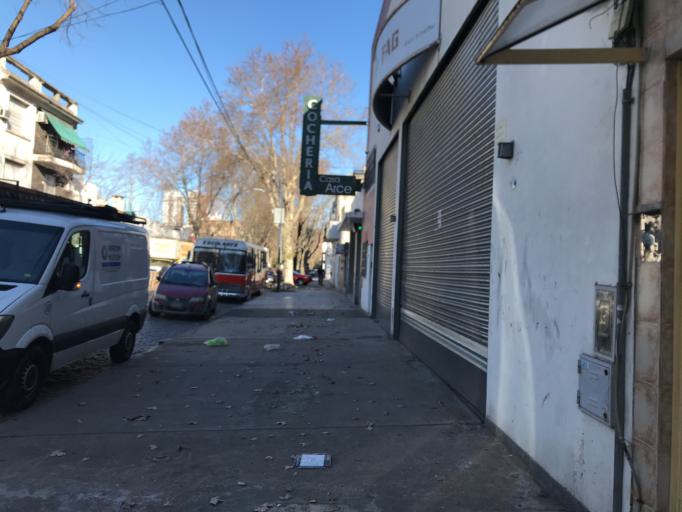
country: AR
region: Buenos Aires F.D.
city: Villa Santa Rita
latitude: -34.6035
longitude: -58.4701
